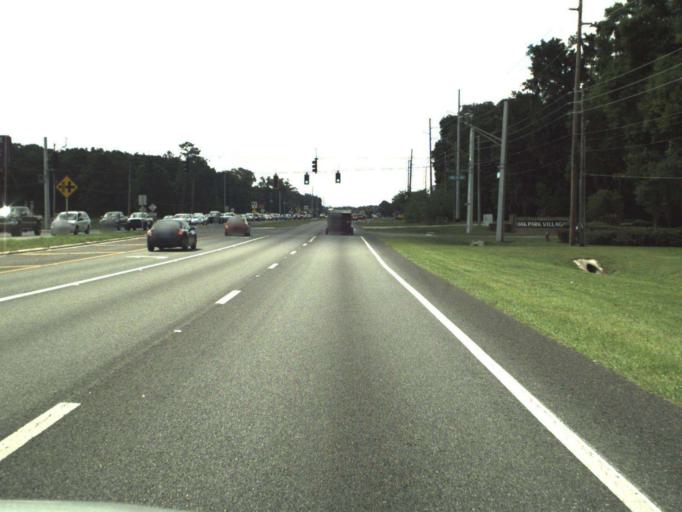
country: US
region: Florida
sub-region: Marion County
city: Ocala
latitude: 29.1547
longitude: -82.0819
